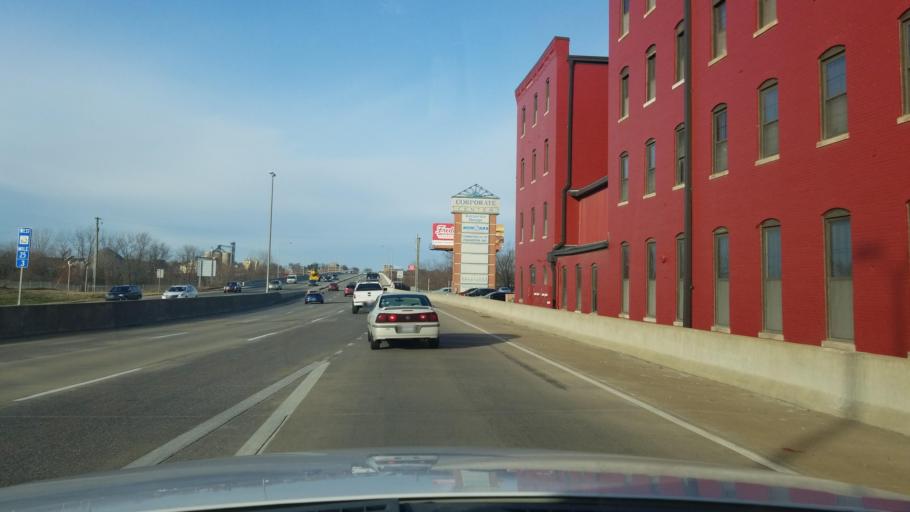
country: US
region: Indiana
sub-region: Vanderburgh County
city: Evansville
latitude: 37.9780
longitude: -87.5842
